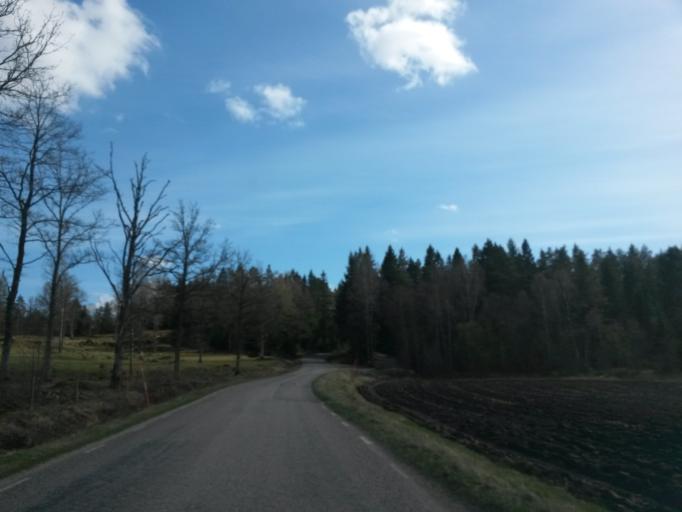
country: SE
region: Vaestra Goetaland
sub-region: Vargarda Kommun
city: Jonstorp
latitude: 58.0048
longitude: 12.7589
